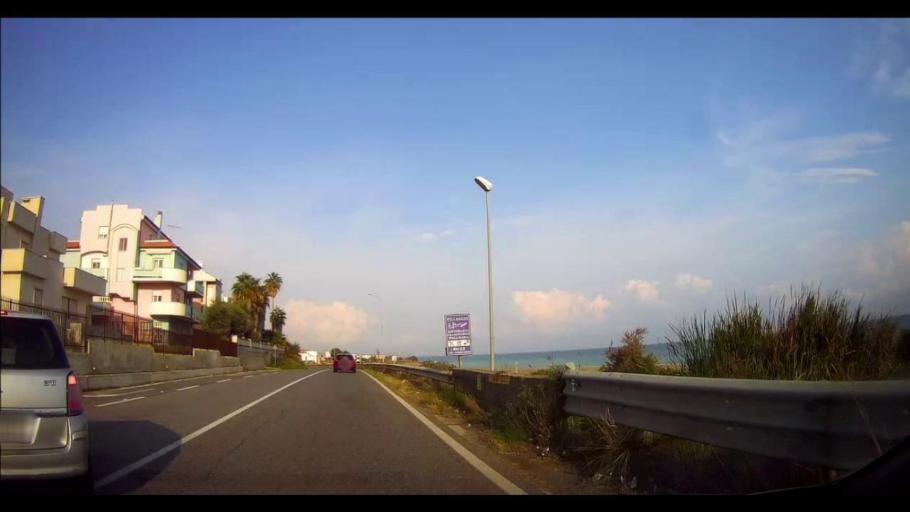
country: IT
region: Calabria
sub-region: Provincia di Cosenza
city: Cariati
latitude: 39.5078
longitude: 16.9349
